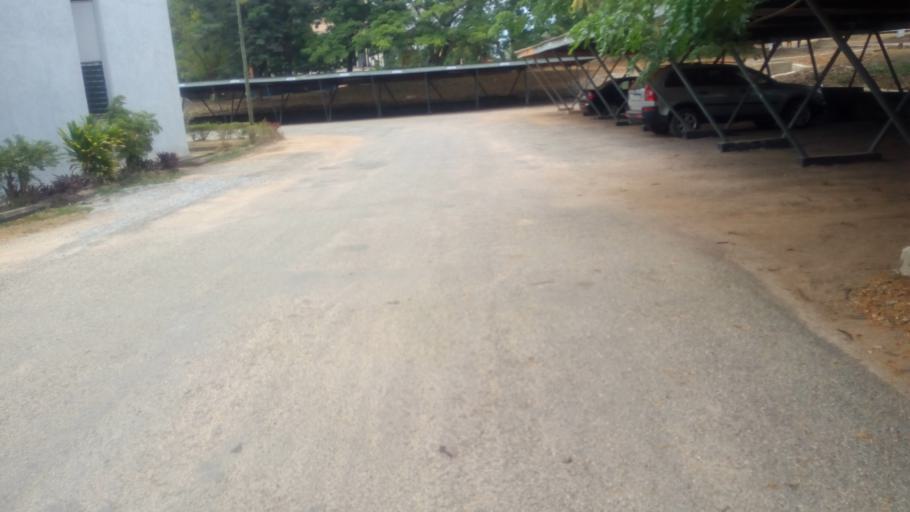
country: GH
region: Central
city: Cape Coast
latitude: 5.1182
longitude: -1.2915
